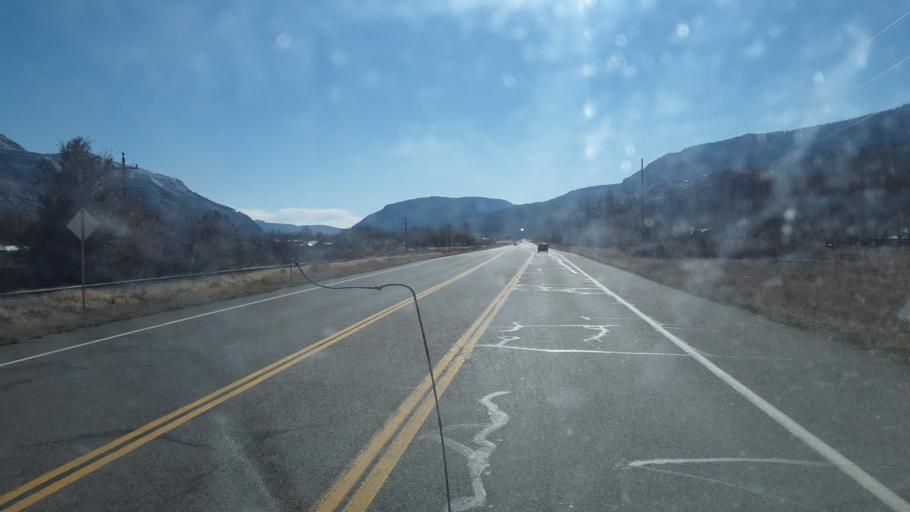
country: US
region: Colorado
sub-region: La Plata County
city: Durango
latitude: 37.4045
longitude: -107.8406
